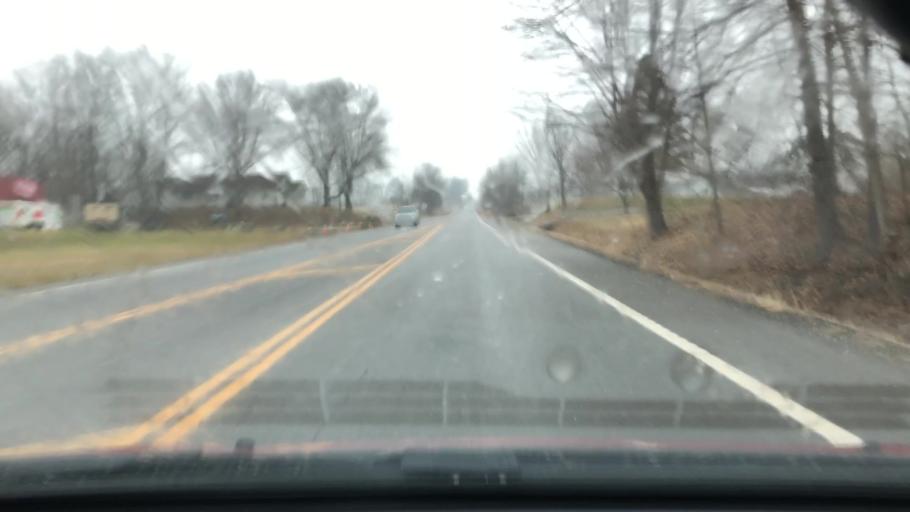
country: US
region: Ohio
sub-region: Wayne County
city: Rittman
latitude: 40.9446
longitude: -81.7444
